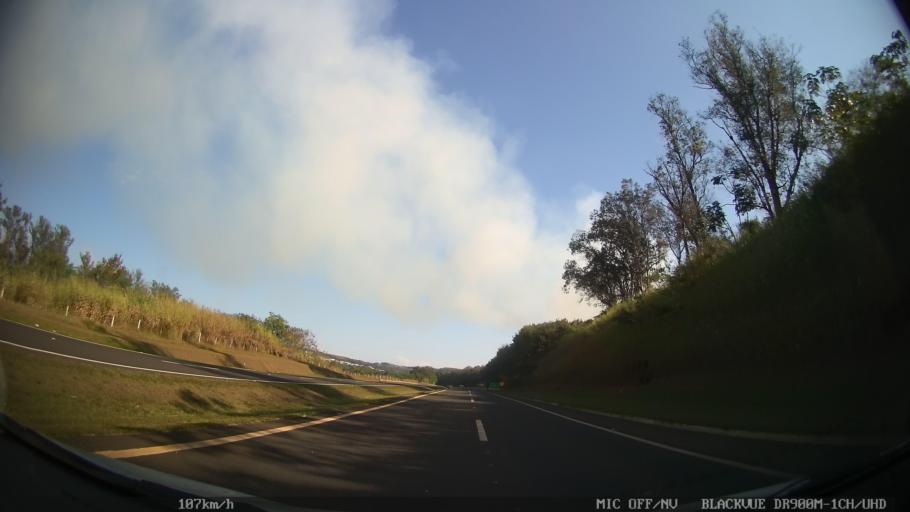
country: BR
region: Sao Paulo
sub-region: Piracicaba
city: Piracicaba
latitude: -22.6926
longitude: -47.5893
